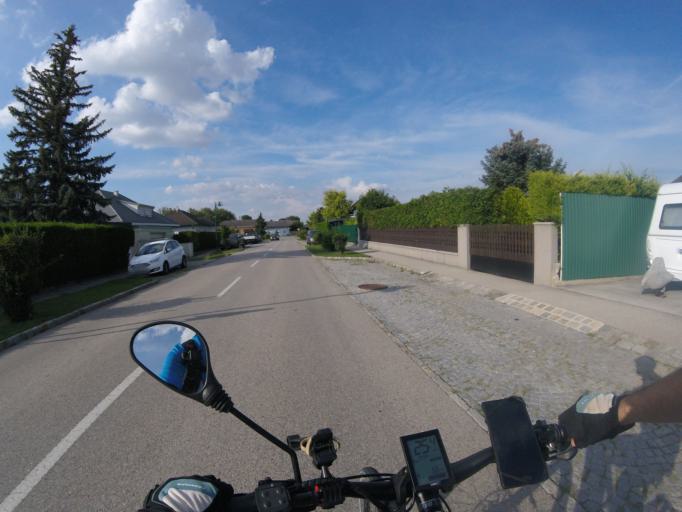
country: AT
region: Lower Austria
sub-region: Politischer Bezirk Baden
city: Trumau
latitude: 47.9917
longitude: 16.3488
